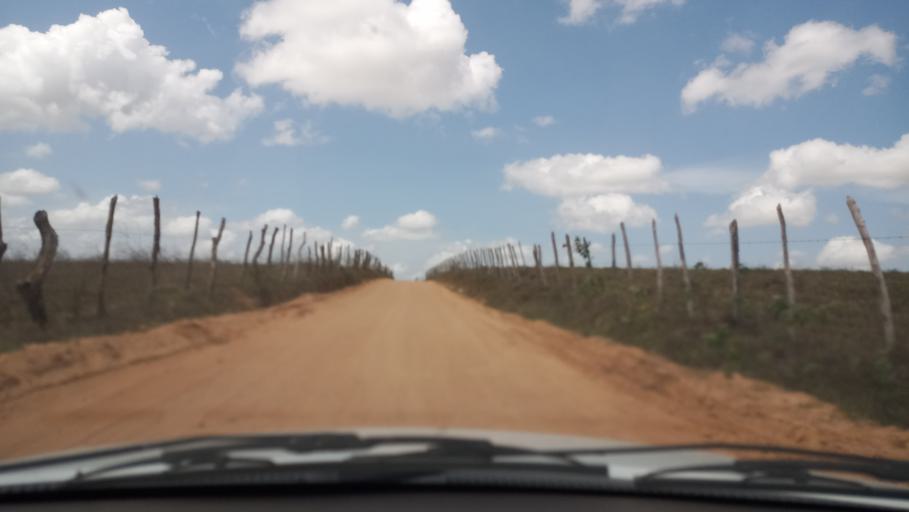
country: BR
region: Rio Grande do Norte
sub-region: Montanhas
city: Montanhas
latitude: -6.3548
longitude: -35.3355
